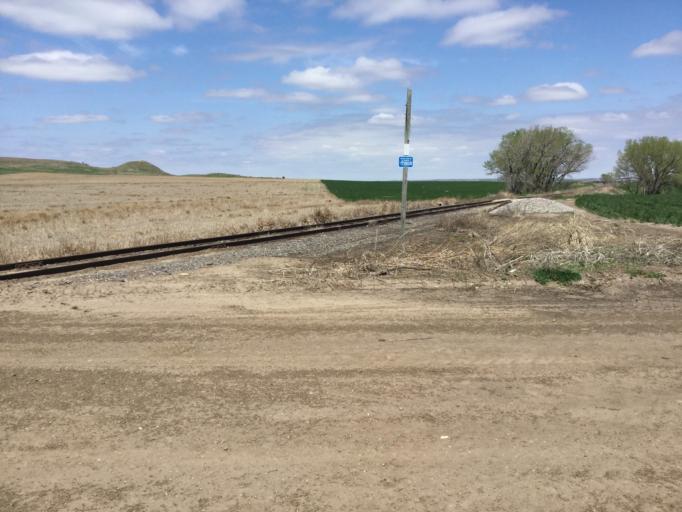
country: US
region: Kansas
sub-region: Osborne County
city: Osborne
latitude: 39.4663
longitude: -98.5917
